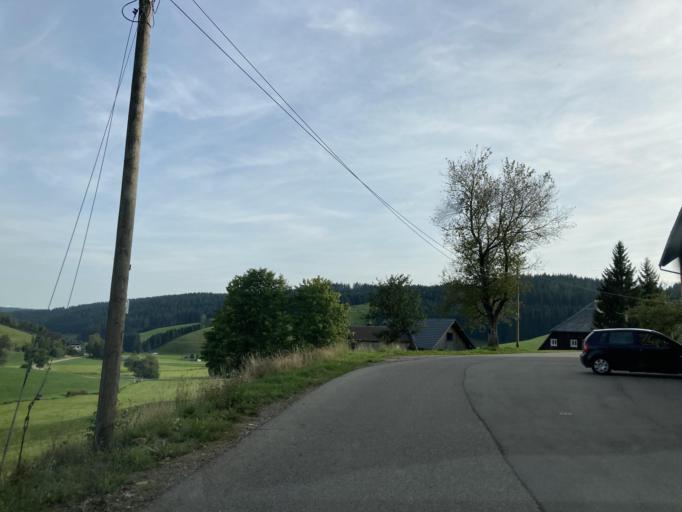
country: DE
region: Baden-Wuerttemberg
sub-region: Freiburg Region
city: Titisee-Neustadt
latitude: 47.9838
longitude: 8.1722
